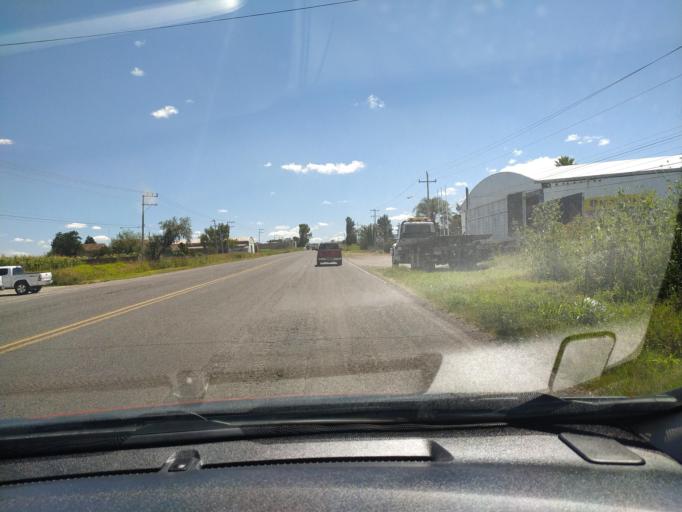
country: MX
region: Jalisco
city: San Miguel el Alto
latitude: 21.0278
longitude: -102.3742
